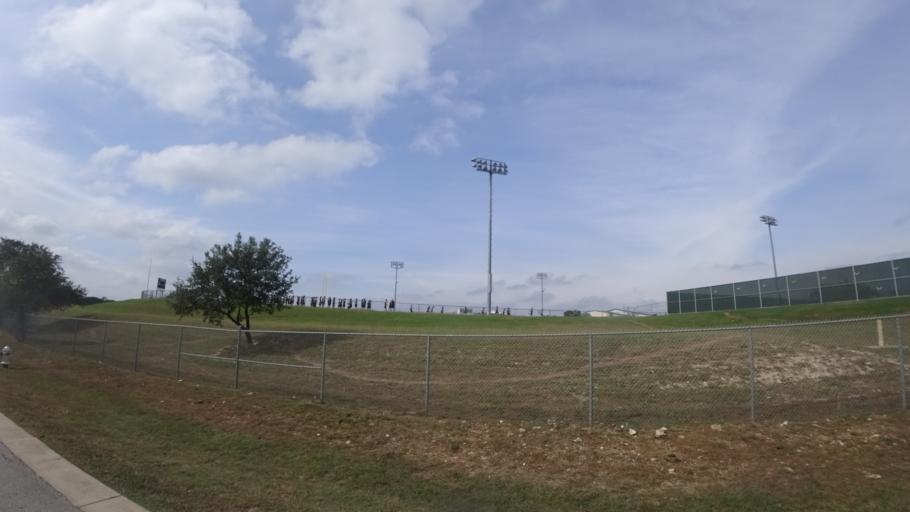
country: US
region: Texas
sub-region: Travis County
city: Hudson Bend
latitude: 30.3896
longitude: -97.9325
